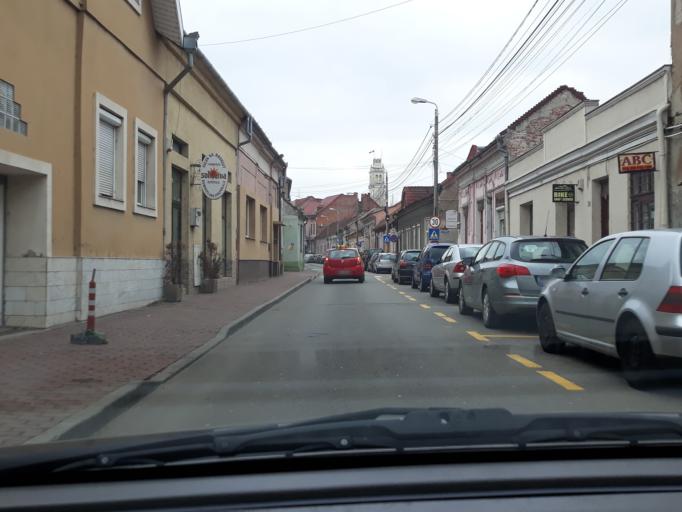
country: RO
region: Bihor
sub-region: Comuna Biharea
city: Oradea
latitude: 47.0594
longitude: 21.9277
